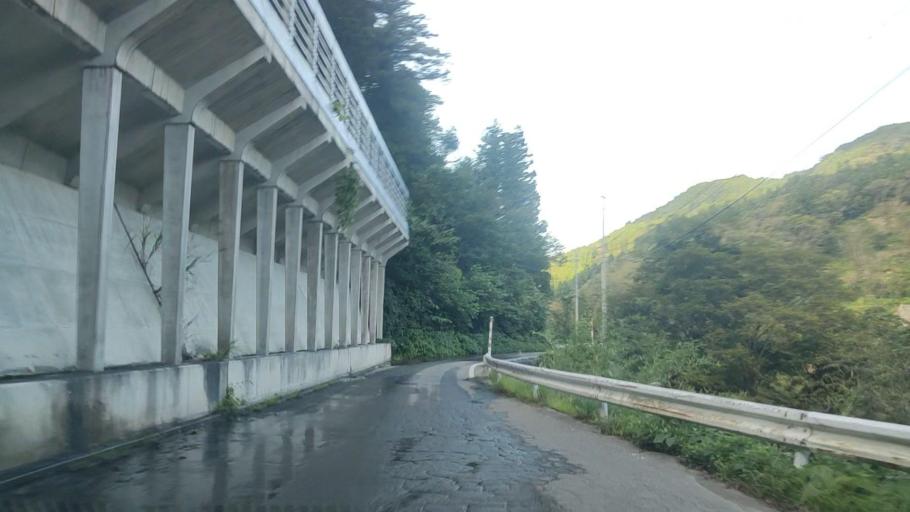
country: JP
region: Toyama
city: Yatsuomachi-higashikumisaka
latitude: 36.4954
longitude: 137.0633
